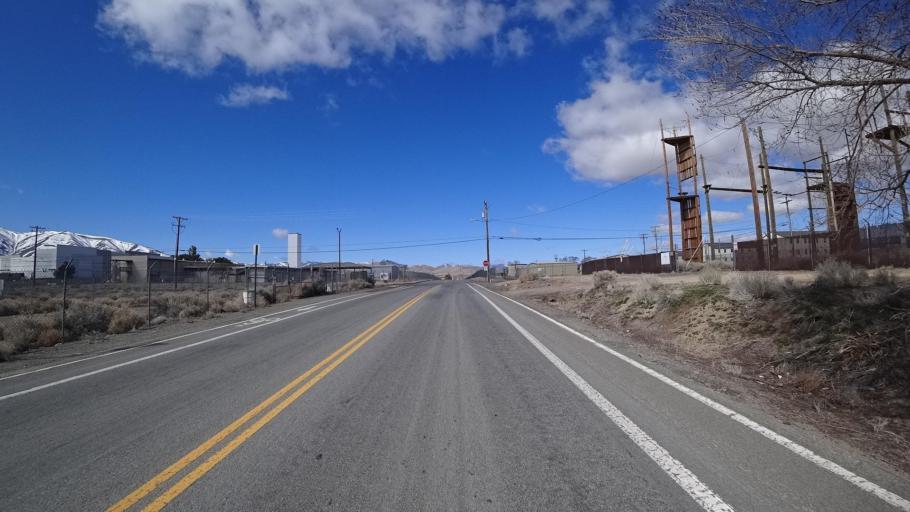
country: US
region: Nevada
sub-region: Washoe County
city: Lemmon Valley
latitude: 39.6570
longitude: -119.8685
